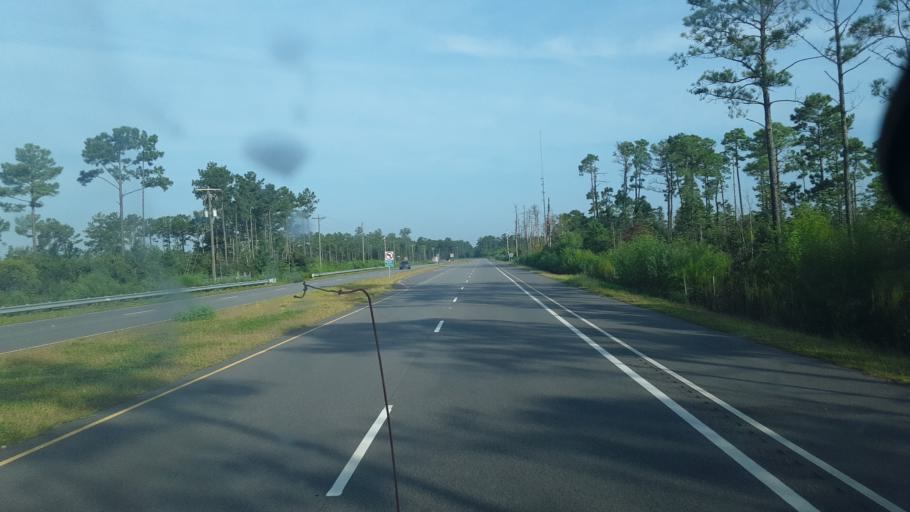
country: US
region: South Carolina
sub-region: Horry County
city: Forestbrook
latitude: 33.8131
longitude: -78.9005
